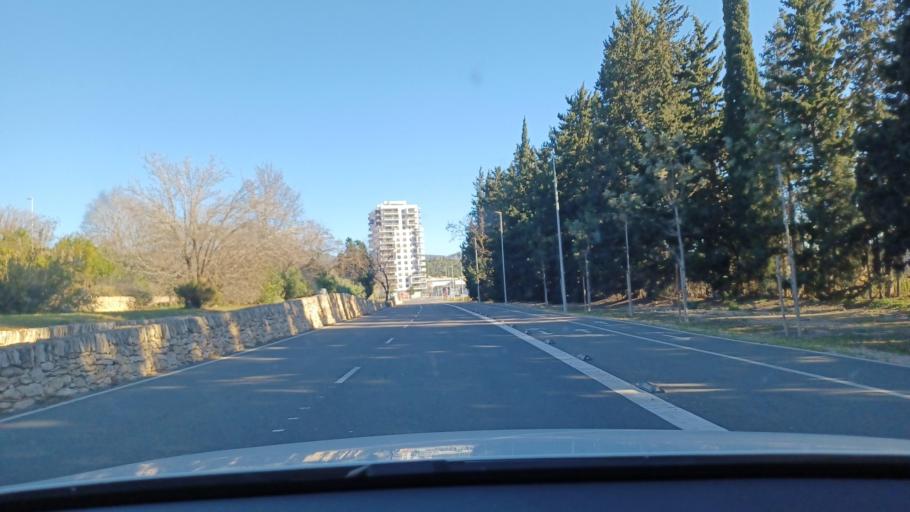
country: ES
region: Catalonia
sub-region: Provincia de Tarragona
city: Tortosa
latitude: 40.8023
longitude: 0.5164
